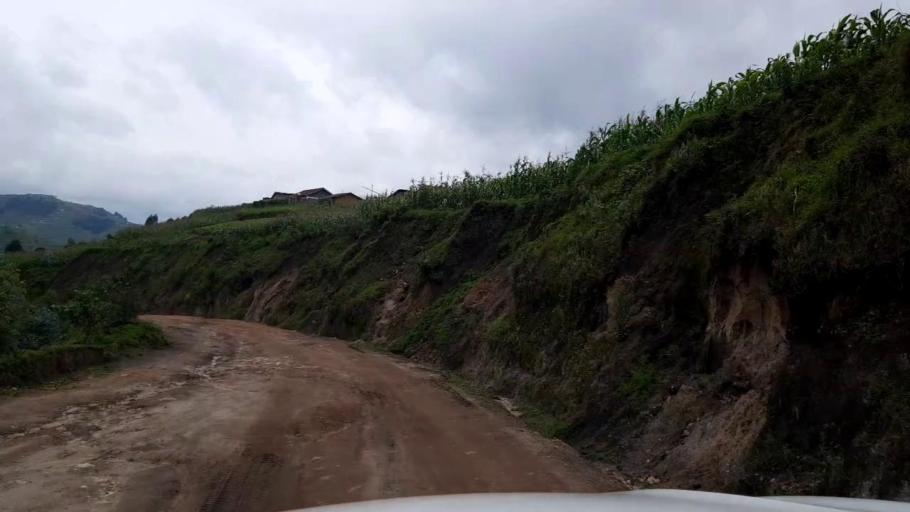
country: RW
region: Western Province
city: Kibuye
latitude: -1.9541
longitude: 29.4150
